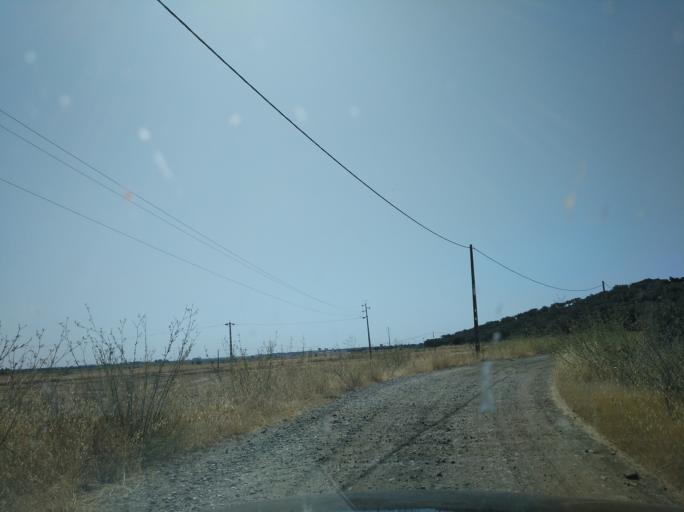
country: PT
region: Portalegre
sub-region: Campo Maior
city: Campo Maior
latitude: 39.0515
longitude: -6.9993
